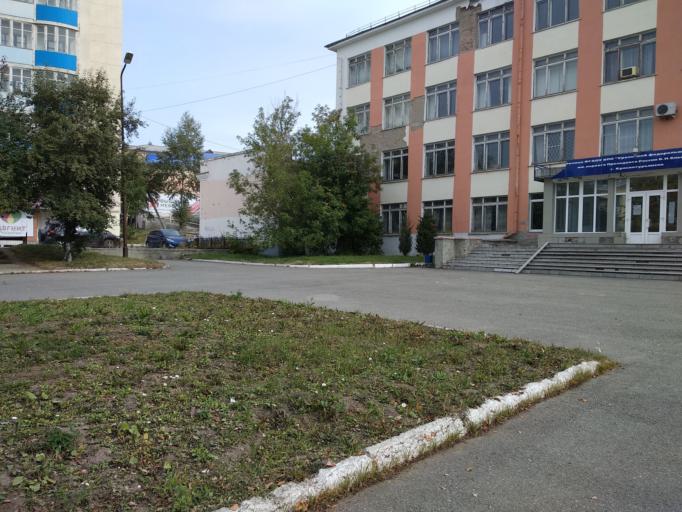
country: RU
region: Sverdlovsk
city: Krasnotur'insk
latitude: 59.7637
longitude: 60.2017
